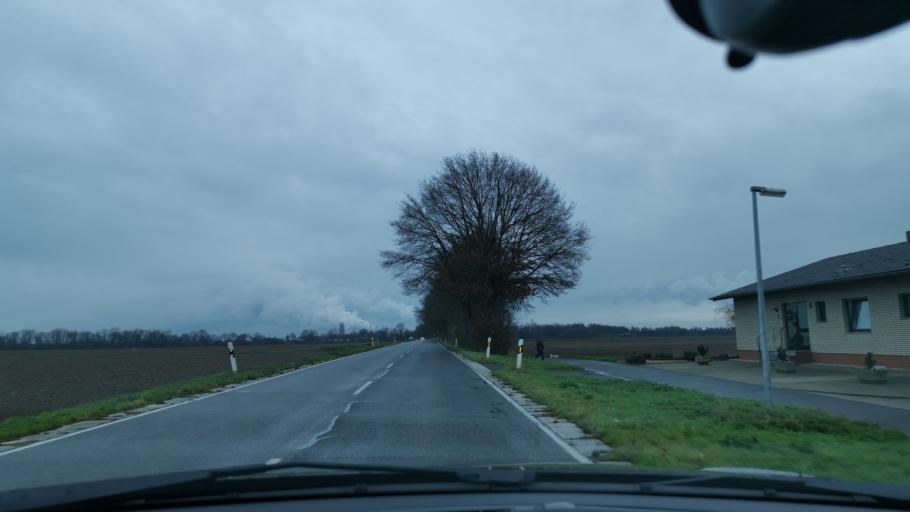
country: DE
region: North Rhine-Westphalia
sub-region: Regierungsbezirk Koln
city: Bedburg
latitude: 50.9992
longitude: 6.5206
